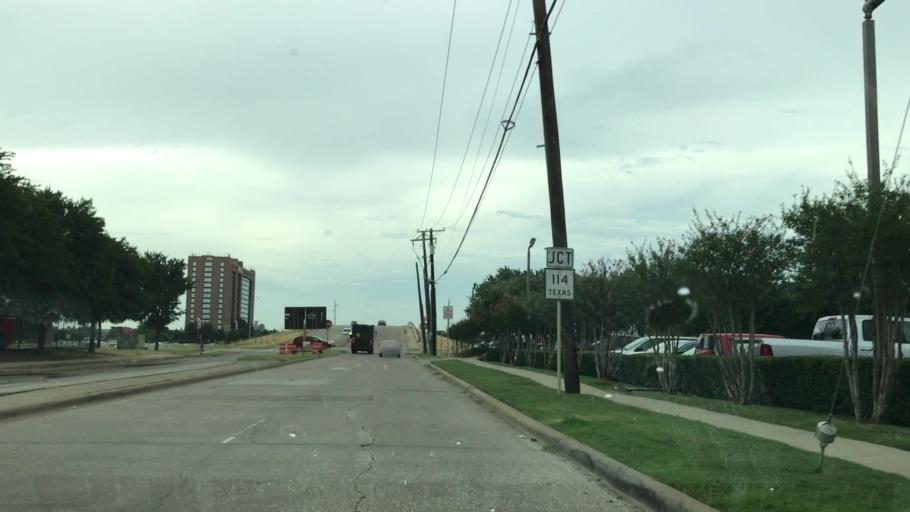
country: US
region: Texas
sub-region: Dallas County
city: Coppell
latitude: 32.9129
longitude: -97.0079
